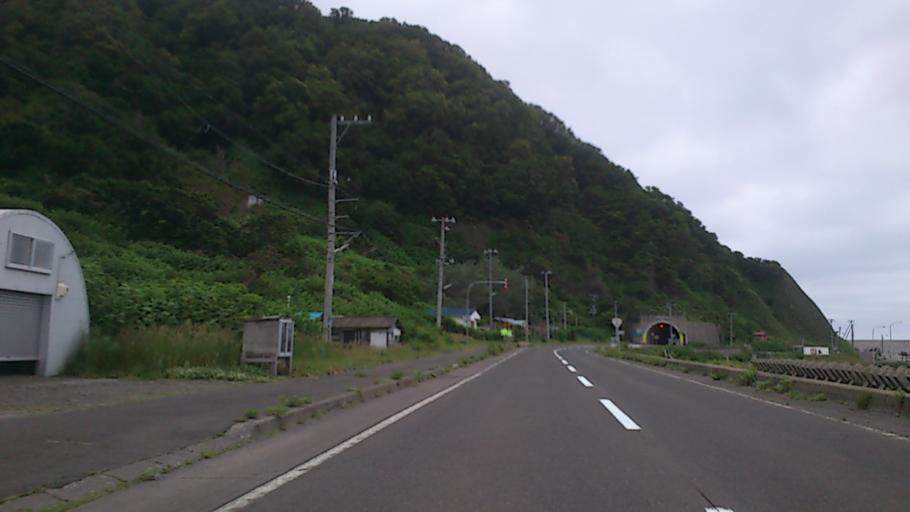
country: JP
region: Hokkaido
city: Iwanai
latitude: 42.6711
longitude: 139.8847
